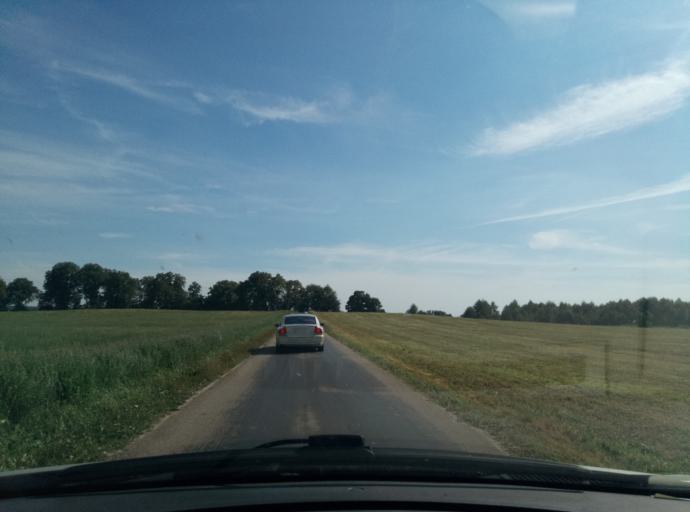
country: PL
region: Kujawsko-Pomorskie
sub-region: Powiat brodnicki
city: Jablonowo Pomorskie
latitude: 53.4114
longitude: 19.2370
